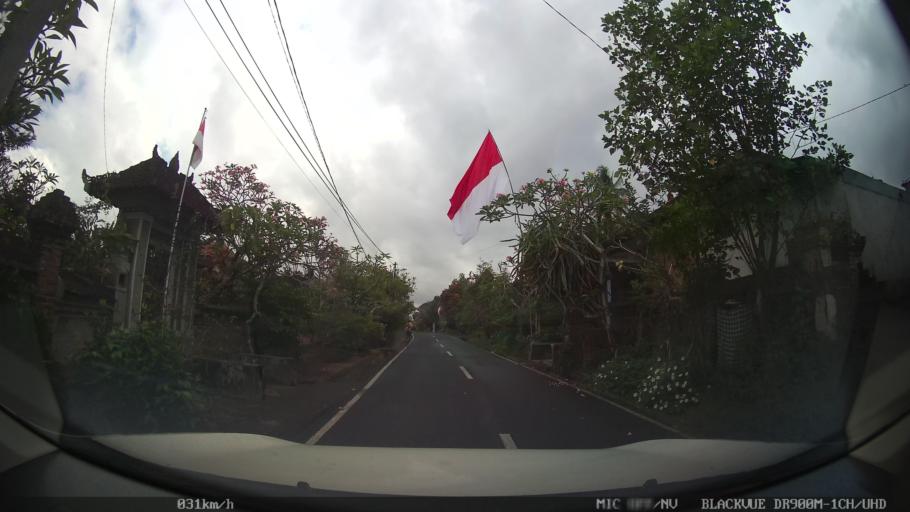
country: ID
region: Bali
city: Banjar Mambalkajanan
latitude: -8.5581
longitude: 115.2085
